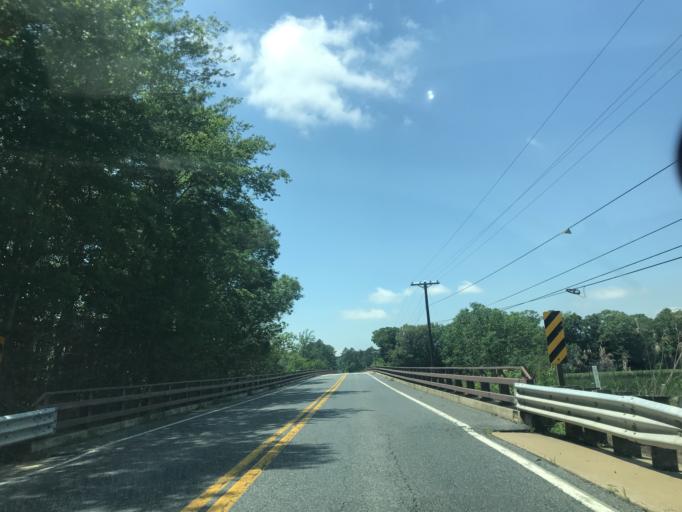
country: US
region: Maryland
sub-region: Dorchester County
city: Hurlock
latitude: 38.6305
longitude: -75.8170
